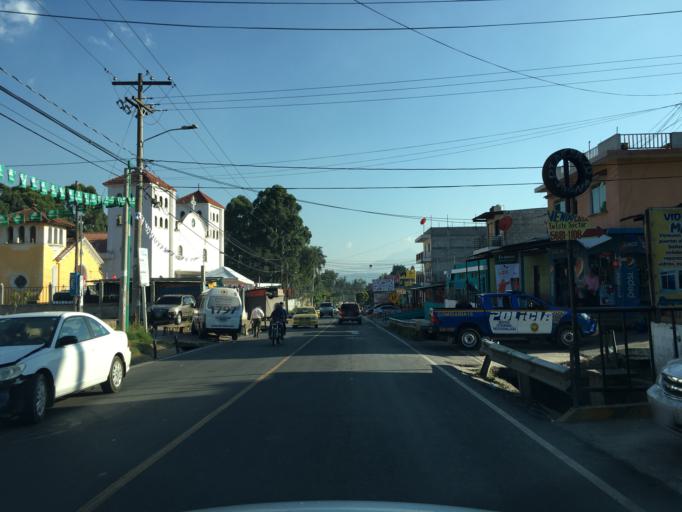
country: GT
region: Guatemala
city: Villa Nueva
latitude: 14.5415
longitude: -90.6158
